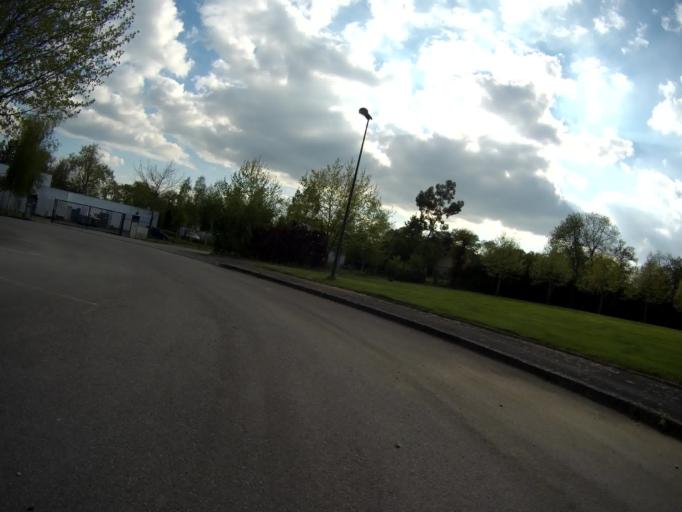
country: FR
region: Brittany
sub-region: Departement d'Ille-et-Vilaine
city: Vern-sur-Seiche
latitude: 48.0432
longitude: -1.6119
